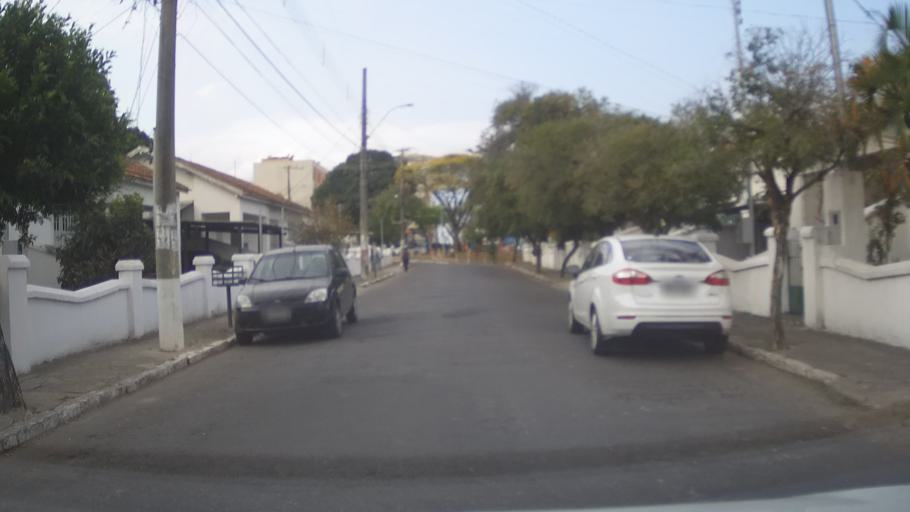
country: BR
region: Minas Gerais
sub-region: Belo Horizonte
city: Belo Horizonte
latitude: -19.8988
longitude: -43.9303
